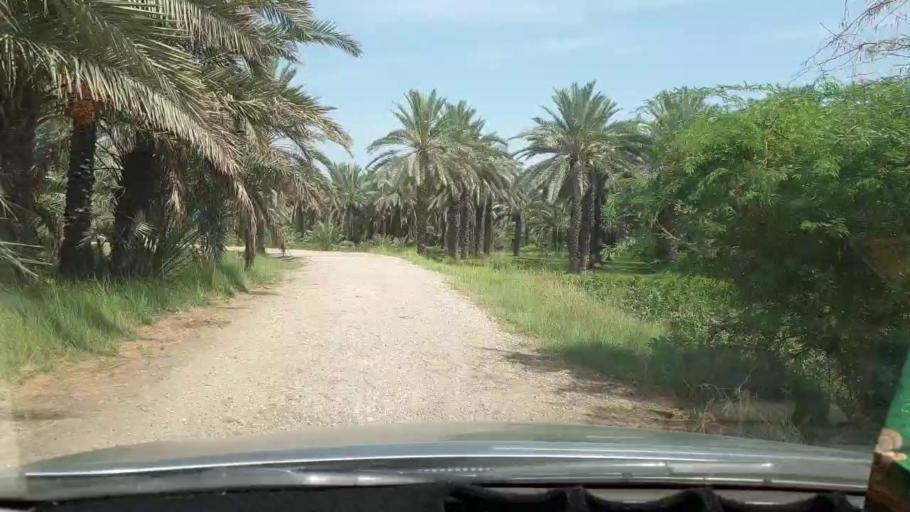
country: PK
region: Sindh
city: Khairpur
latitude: 27.4697
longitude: 68.7483
